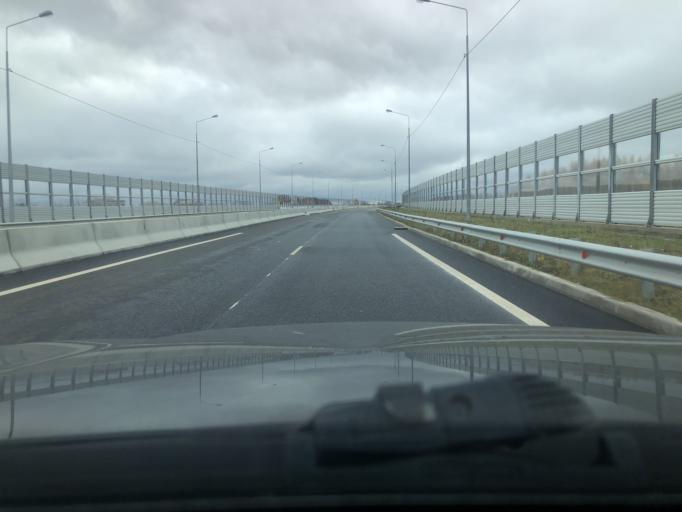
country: RU
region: Moskovskaya
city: Semkhoz
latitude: 56.3158
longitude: 38.0908
